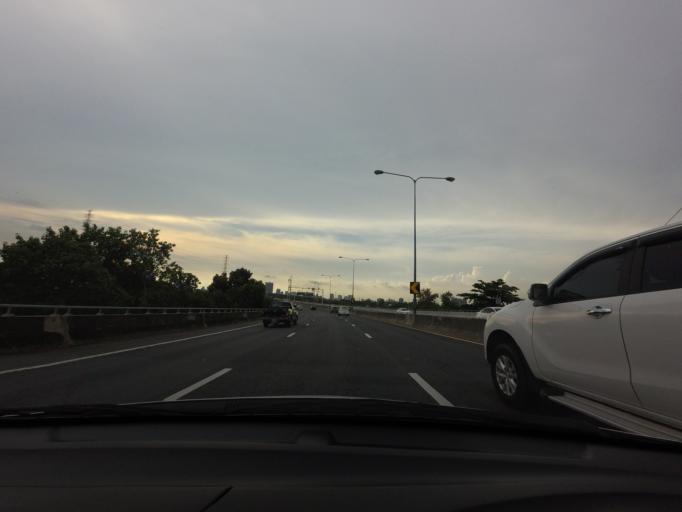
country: TH
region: Bangkok
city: Watthana
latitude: 13.7497
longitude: 100.6039
